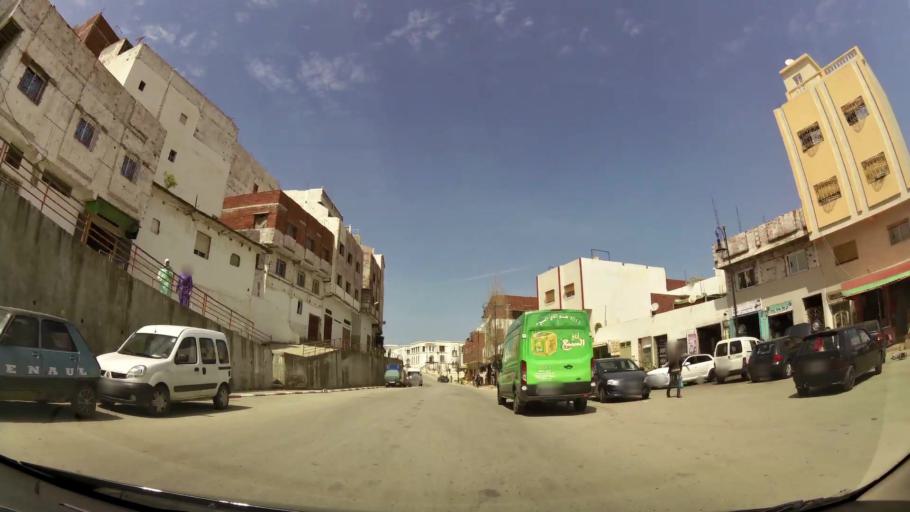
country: MA
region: Tanger-Tetouan
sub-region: Tanger-Assilah
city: Tangier
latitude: 35.7380
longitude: -5.8229
